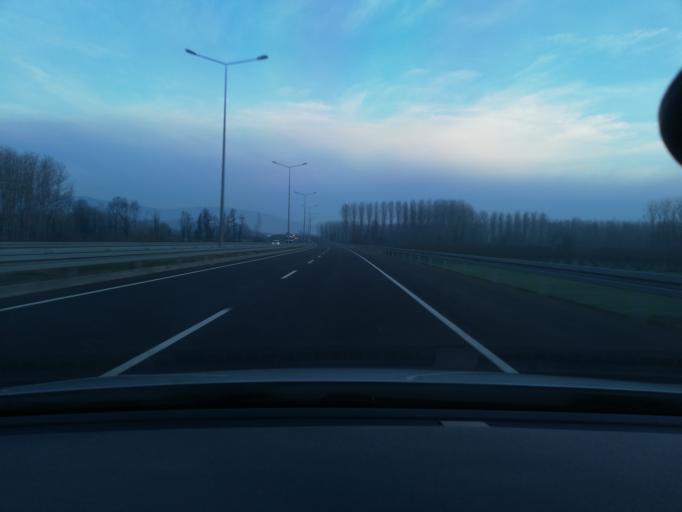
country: TR
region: Duzce
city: Duzce
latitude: 40.8117
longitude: 31.1692
